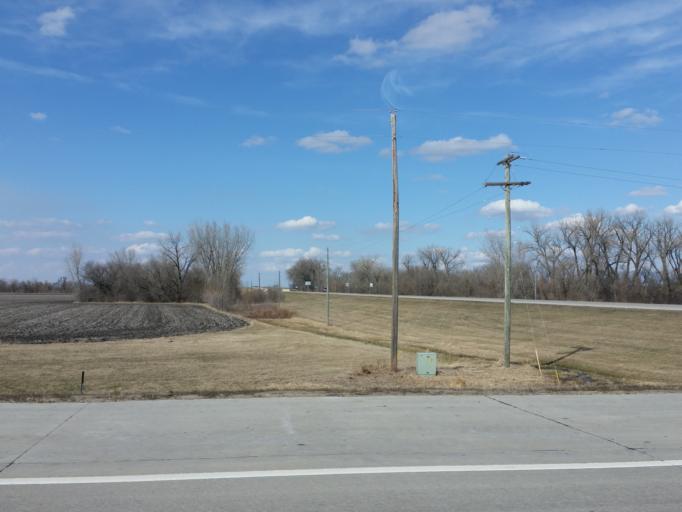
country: US
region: Minnesota
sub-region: Lac qui Parle County
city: Madison
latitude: 44.9359
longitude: -96.1968
